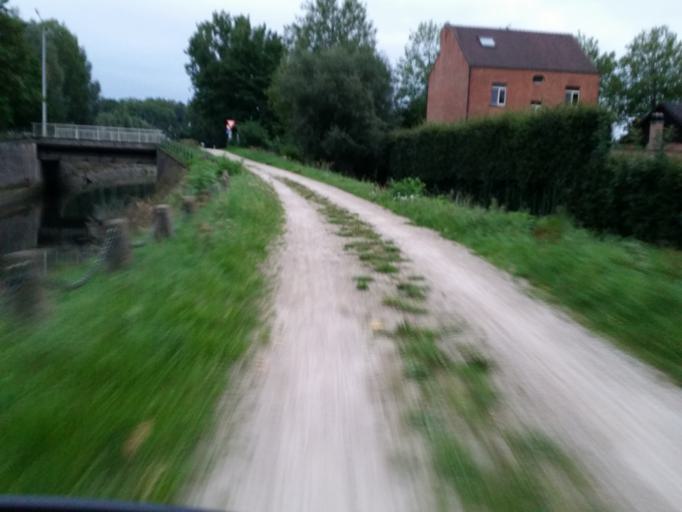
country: BE
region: Flanders
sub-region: Provincie Vlaams-Brabant
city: Zemst
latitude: 50.9876
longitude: 4.4697
